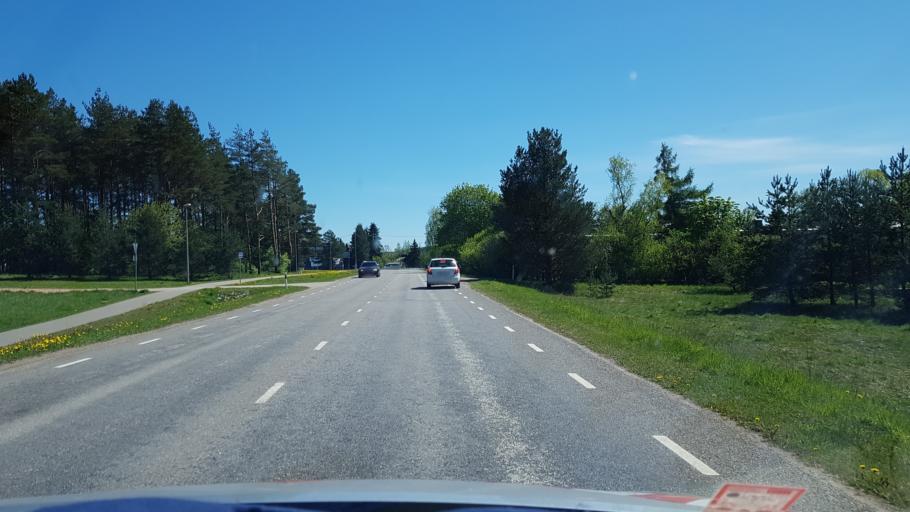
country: EE
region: Tartu
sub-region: UElenurme vald
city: Ulenurme
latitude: 58.3019
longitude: 26.8641
